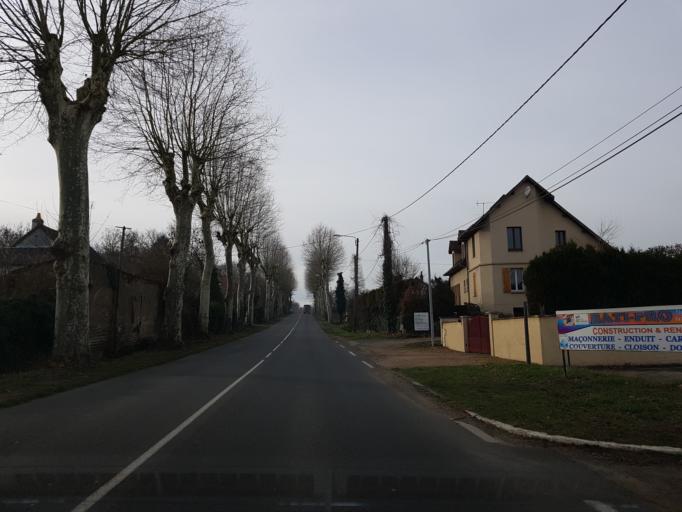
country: FR
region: Auvergne
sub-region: Departement de l'Allier
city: Neuvy
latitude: 46.5577
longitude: 3.3084
